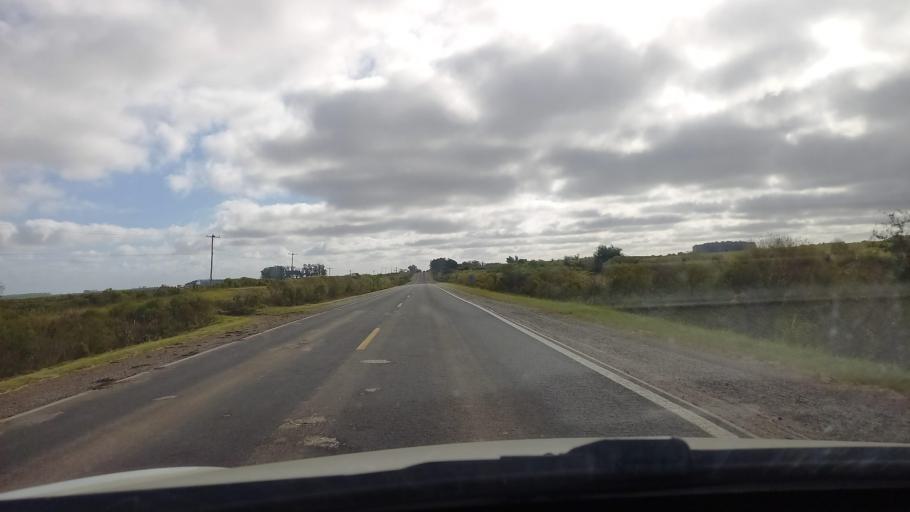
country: BR
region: Rio Grande do Sul
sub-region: Dom Pedrito
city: Dom Pedrito
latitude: -30.9057
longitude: -54.8227
